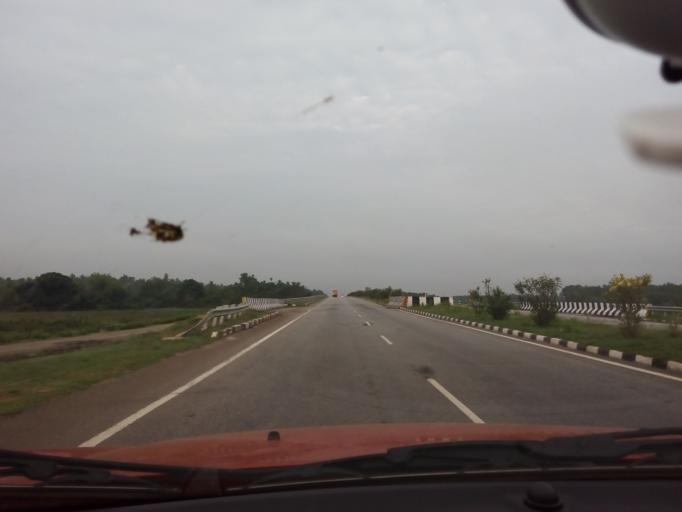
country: IN
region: Karnataka
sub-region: Tumkur
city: Kunigal
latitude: 13.0051
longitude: 76.9962
